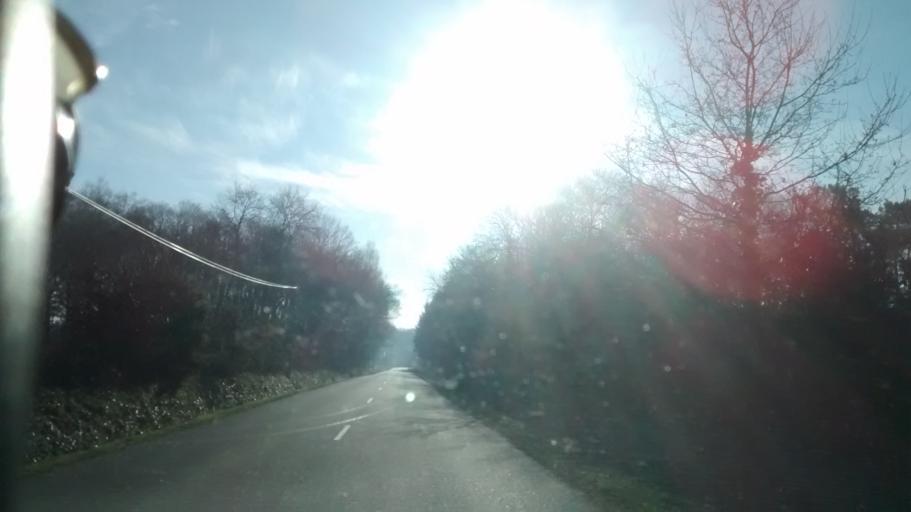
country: FR
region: Brittany
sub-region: Departement d'Ille-et-Vilaine
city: La Bouexiere
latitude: 48.1582
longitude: -1.4137
